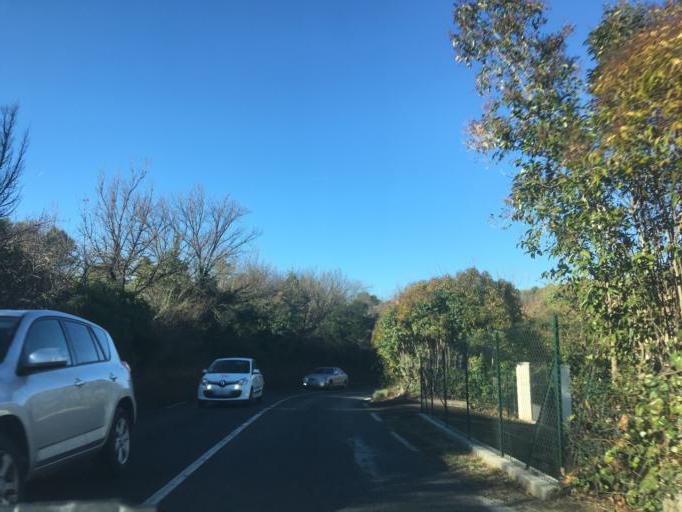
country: FR
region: Provence-Alpes-Cote d'Azur
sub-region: Departement du Var
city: Flayosc
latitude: 43.5365
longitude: 6.3984
